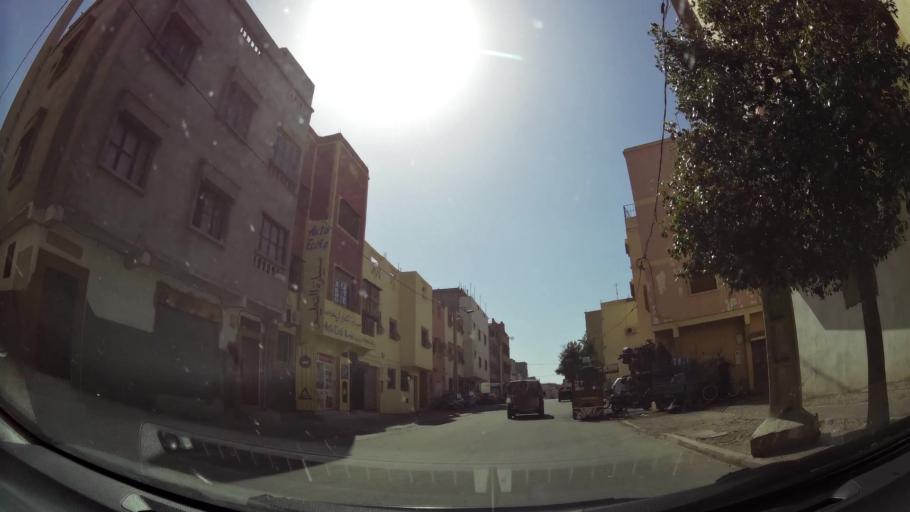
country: MA
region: Souss-Massa-Draa
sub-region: Inezgane-Ait Mellou
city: Inezgane
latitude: 30.3560
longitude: -9.5469
